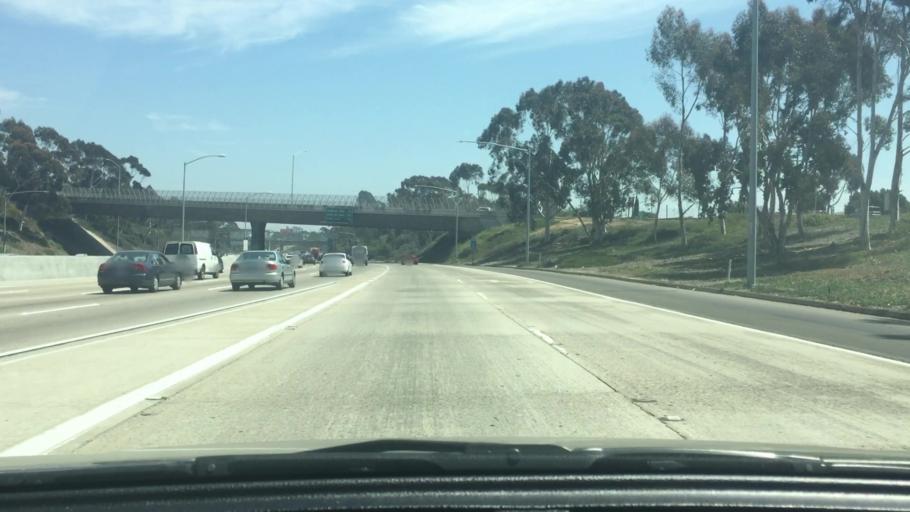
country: US
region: California
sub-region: San Diego County
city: National City
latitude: 32.7123
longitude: -117.1023
